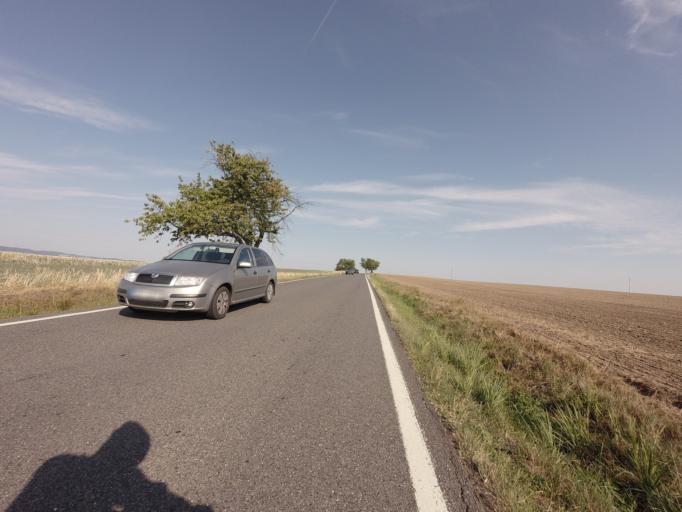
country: CZ
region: Jihocesky
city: Bernartice
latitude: 49.3072
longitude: 14.3792
